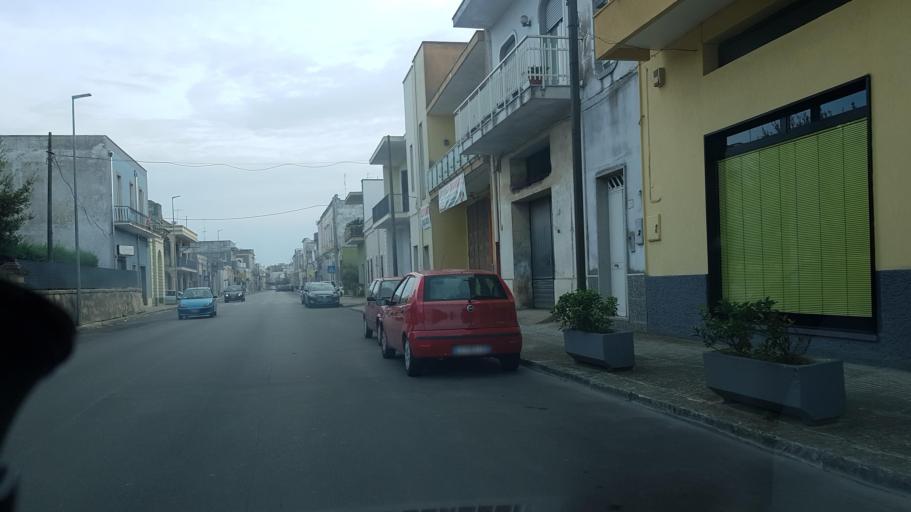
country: IT
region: Apulia
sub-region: Provincia di Lecce
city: Trepuzzi
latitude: 40.4089
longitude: 18.0678
